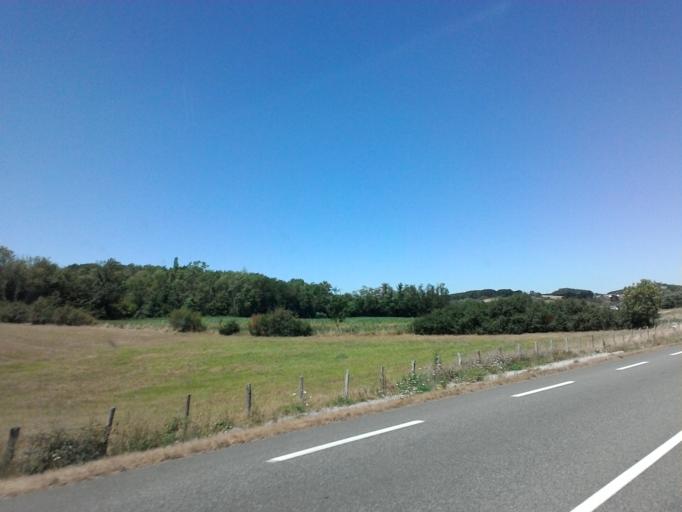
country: FR
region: Franche-Comte
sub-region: Departement du Jura
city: Montmorot
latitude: 46.6507
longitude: 5.5083
